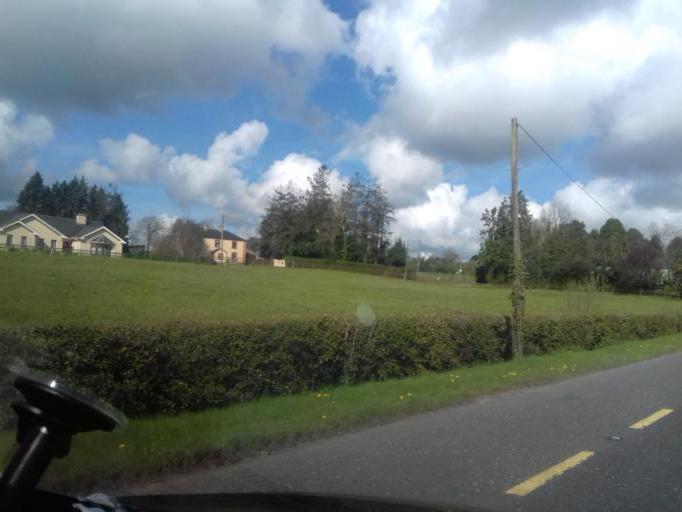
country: IE
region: Ulster
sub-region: An Cabhan
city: Virginia
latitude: 53.8755
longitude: -7.1251
